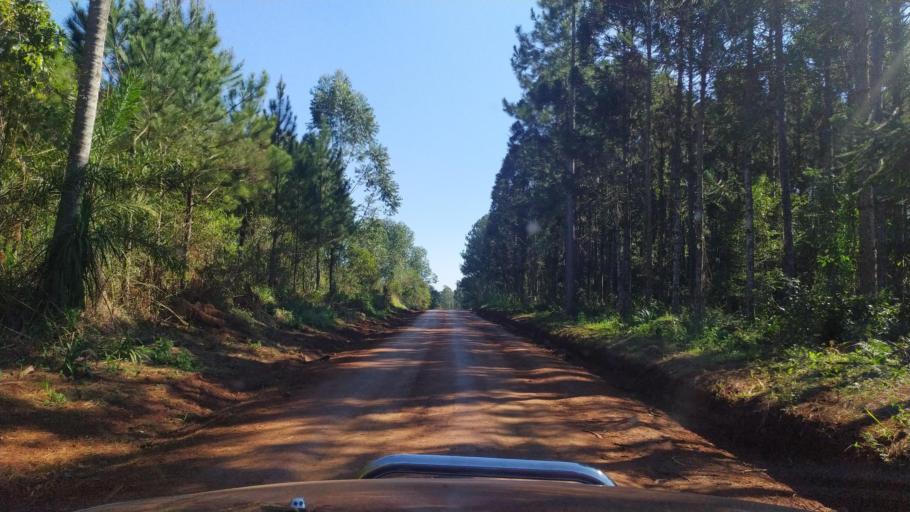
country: AR
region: Misiones
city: El Alcazar
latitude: -26.7340
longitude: -54.6685
